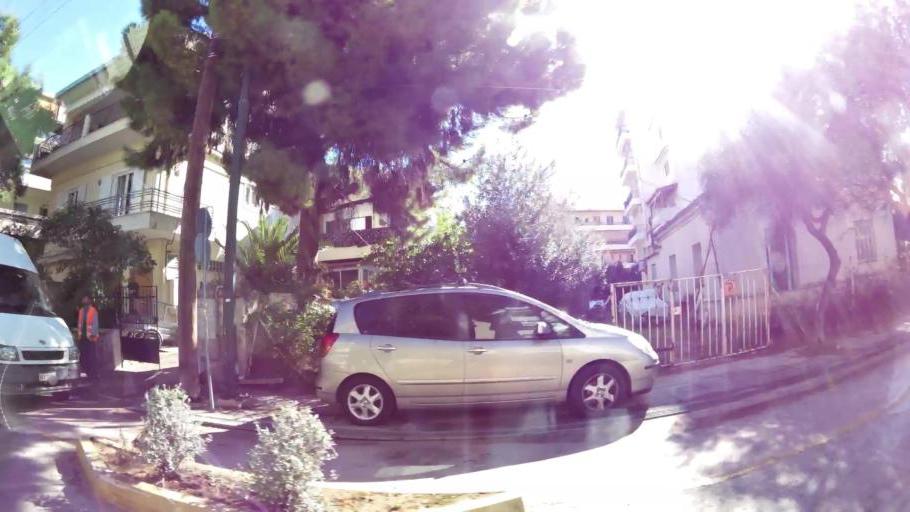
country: GR
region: Attica
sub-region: Nomarchia Athinas
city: Khalandrion
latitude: 38.0232
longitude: 23.8112
